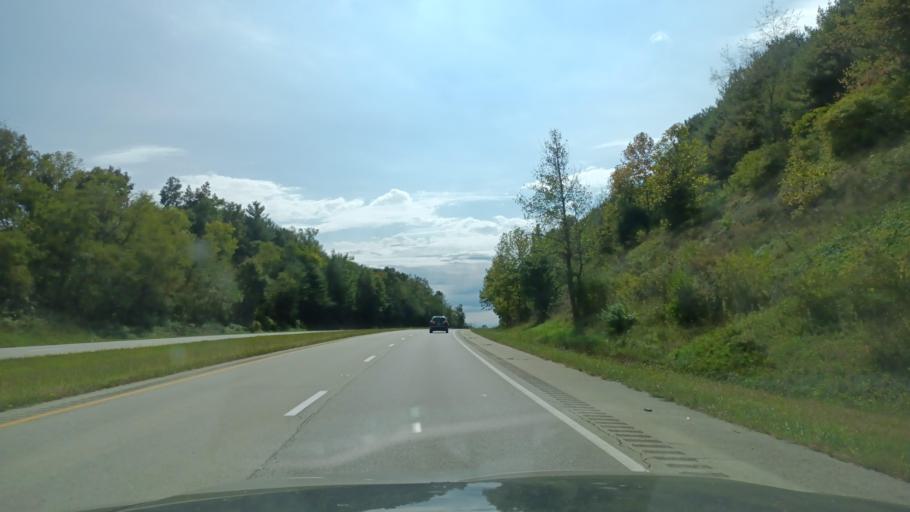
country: US
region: Ohio
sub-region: Athens County
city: Athens
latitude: 39.2599
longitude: -82.1664
